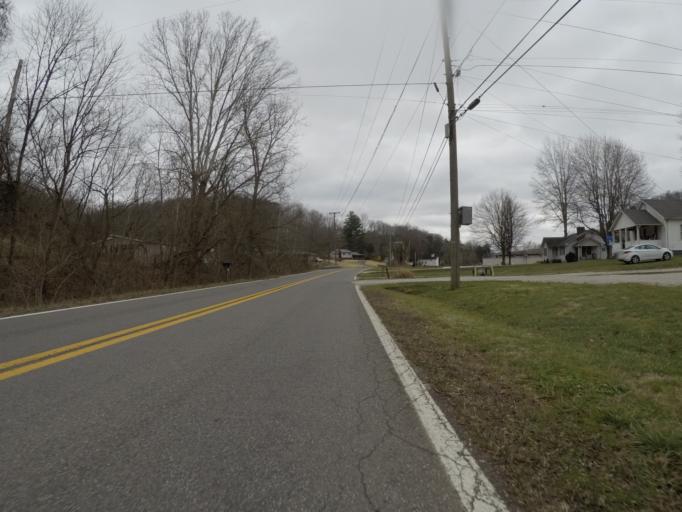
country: US
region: West Virginia
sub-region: Cabell County
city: Barboursville
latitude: 38.4290
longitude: -82.2924
